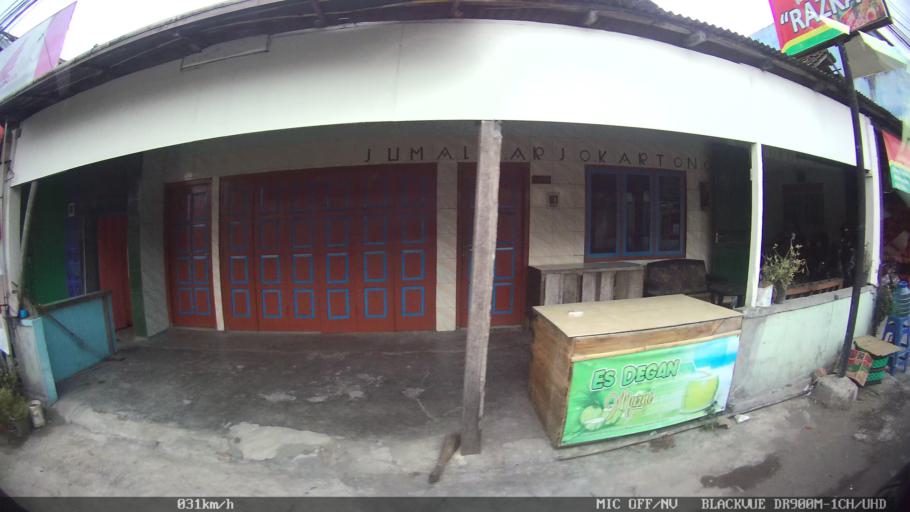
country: ID
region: Daerah Istimewa Yogyakarta
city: Depok
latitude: -7.8246
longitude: 110.4142
